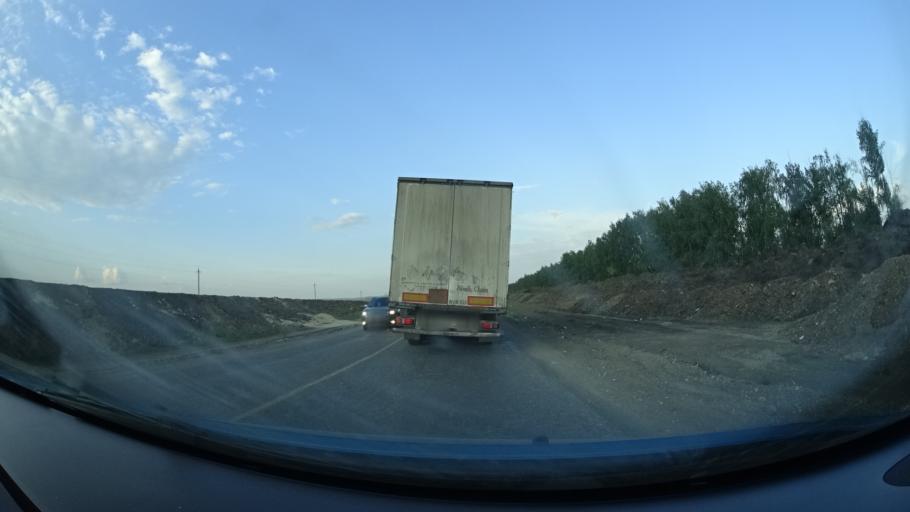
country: RU
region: Samara
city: Kamyshla
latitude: 54.0451
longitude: 52.0025
